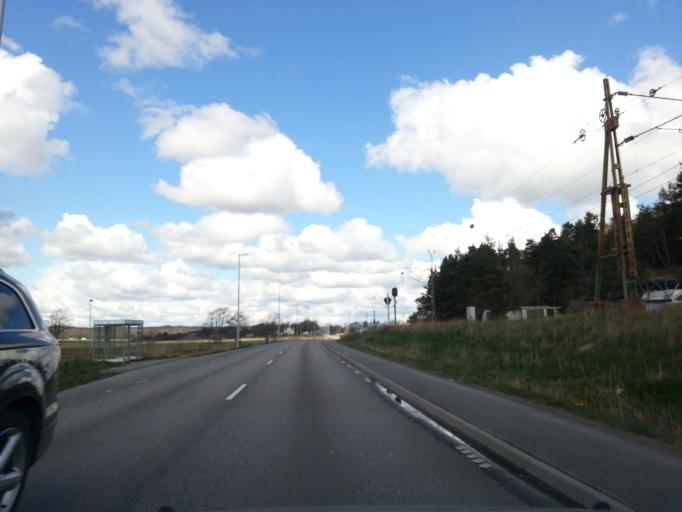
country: SE
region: Vaestra Goetaland
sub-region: Kungalvs Kommun
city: Kungalv
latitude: 57.8062
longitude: 11.9099
